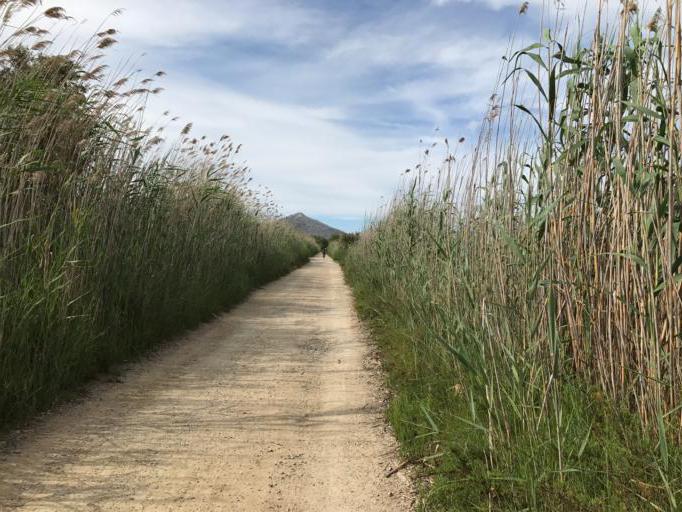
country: ES
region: Balearic Islands
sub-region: Illes Balears
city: Port d'Alcudia
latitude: 39.7958
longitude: 3.1117
